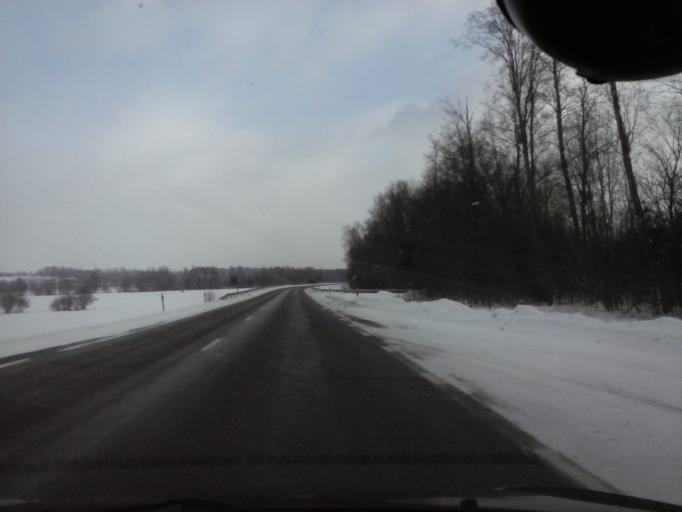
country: EE
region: Viljandimaa
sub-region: Viljandi linn
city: Viljandi
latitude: 58.3519
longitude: 25.4589
